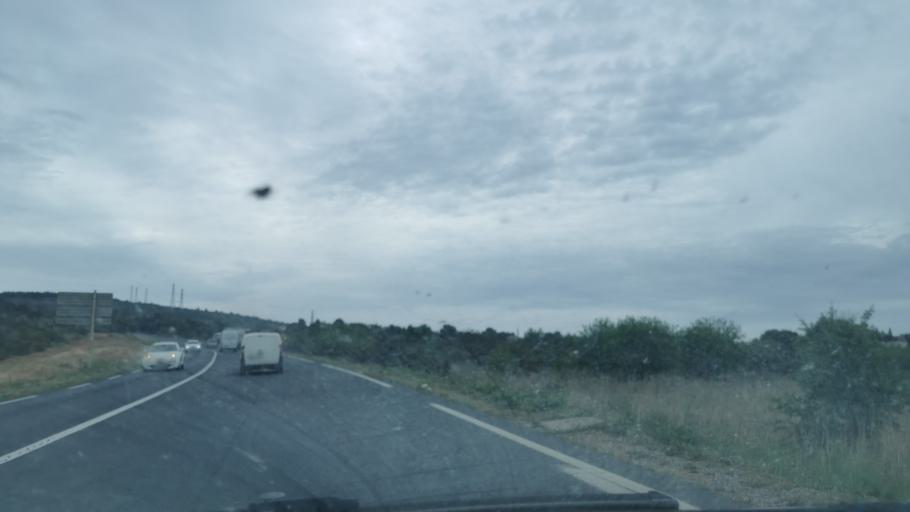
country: FR
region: Languedoc-Roussillon
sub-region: Departement de l'Herault
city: Balaruc-le-Vieux
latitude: 43.4593
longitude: 3.6956
